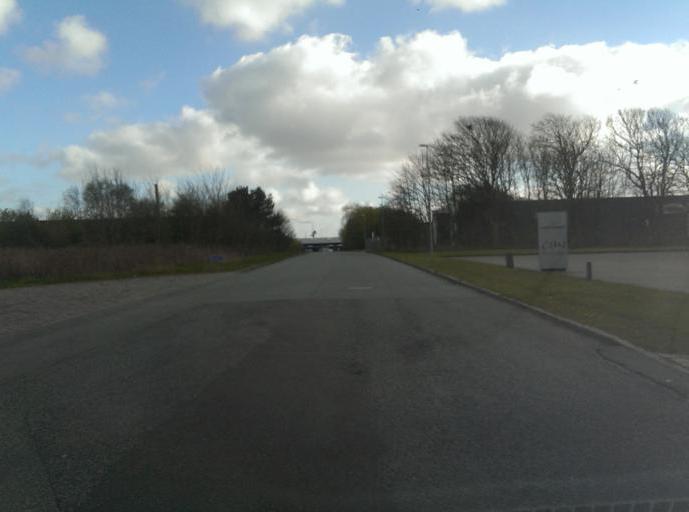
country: DK
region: South Denmark
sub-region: Esbjerg Kommune
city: Esbjerg
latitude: 55.5151
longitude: 8.4639
